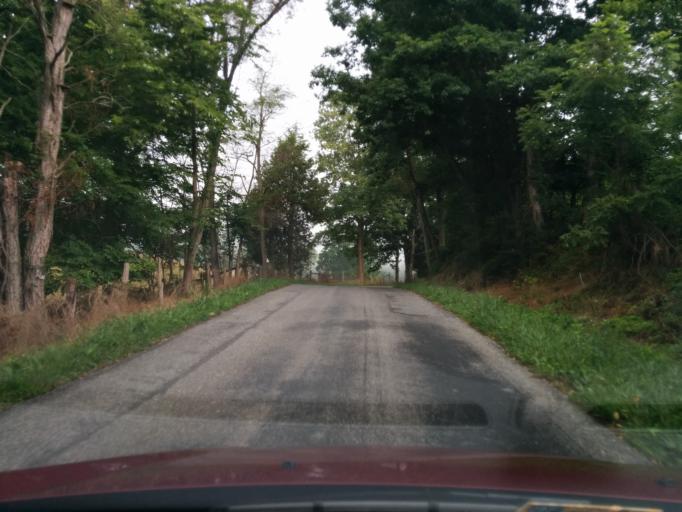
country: US
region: Virginia
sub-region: City of Lexington
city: Lexington
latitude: 37.7854
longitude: -79.4668
